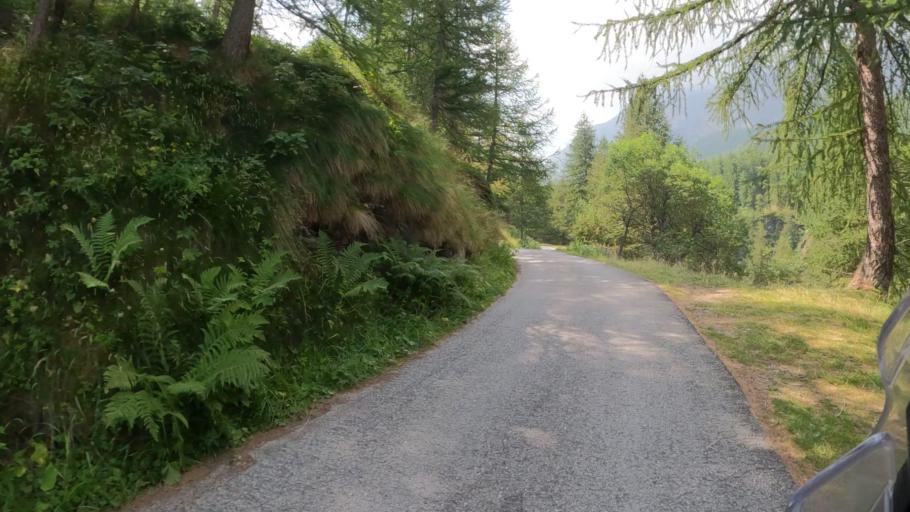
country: IT
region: Piedmont
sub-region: Provincia di Cuneo
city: Marmora
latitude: 44.4206
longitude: 7.1033
